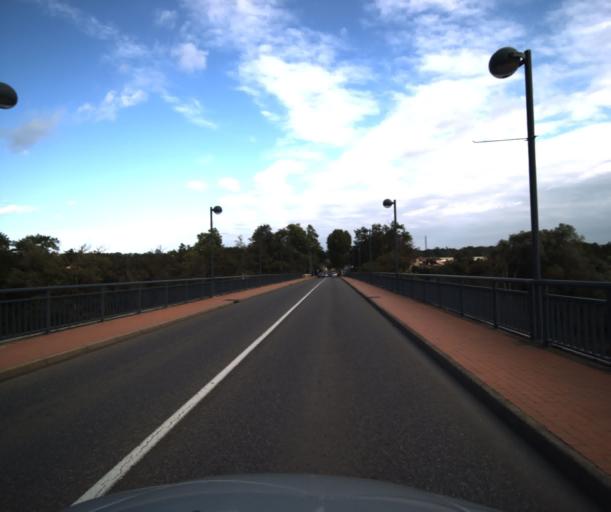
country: FR
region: Midi-Pyrenees
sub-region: Departement de la Haute-Garonne
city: Muret
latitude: 43.4583
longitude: 1.3273
